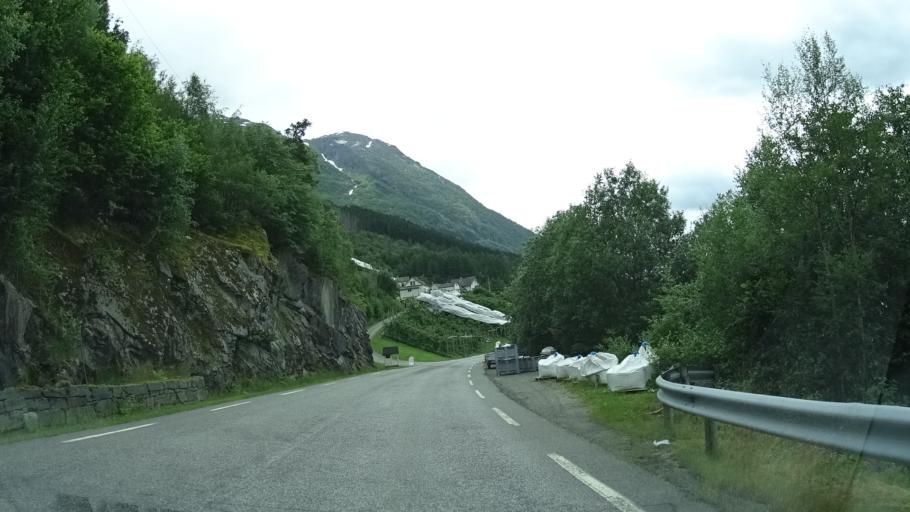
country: NO
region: Hordaland
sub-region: Granvin
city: Granvin
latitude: 60.4520
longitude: 6.8076
